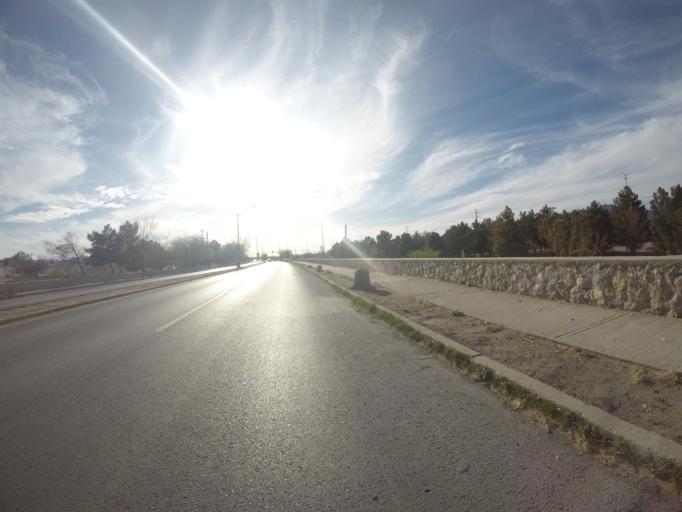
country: US
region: Texas
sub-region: El Paso County
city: El Paso
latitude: 31.7546
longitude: -106.4461
